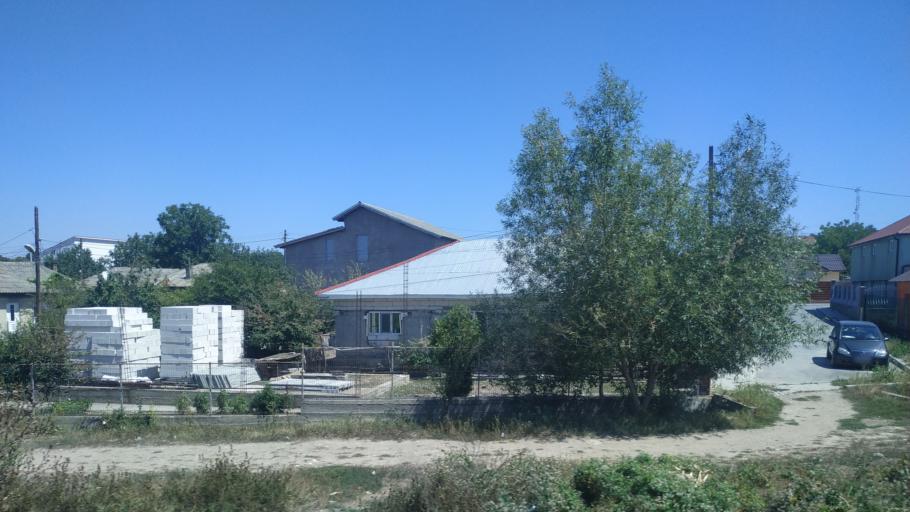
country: RO
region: Constanta
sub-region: Oras Murfatlar
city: Murfatlar
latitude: 44.1778
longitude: 28.4011
